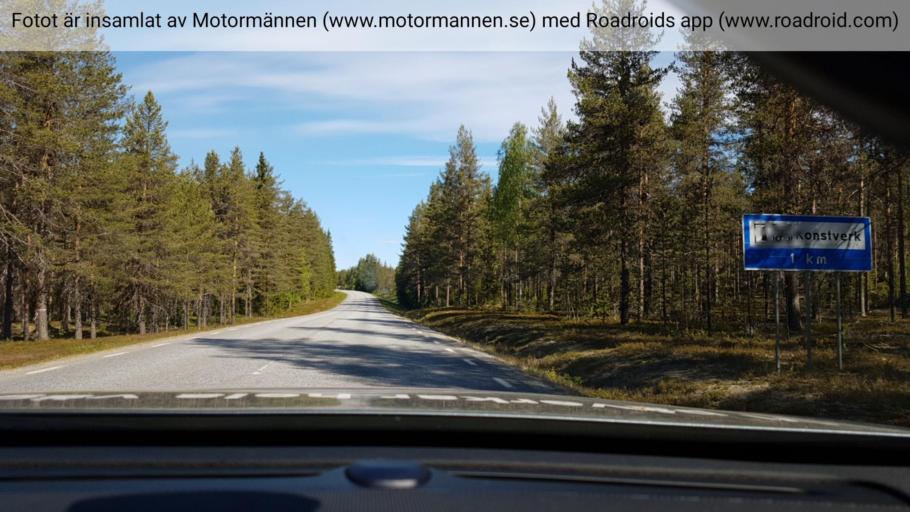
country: SE
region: Vaesterbotten
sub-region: Bjurholms Kommun
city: Bjurholm
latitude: 63.9807
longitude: 18.8107
